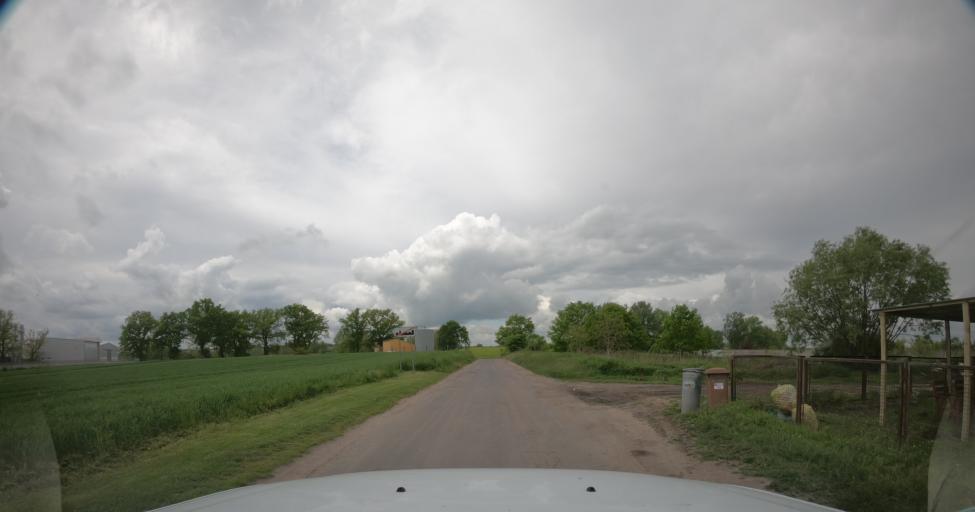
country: PL
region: West Pomeranian Voivodeship
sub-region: Powiat pyrzycki
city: Kozielice
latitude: 53.0782
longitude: 14.8784
